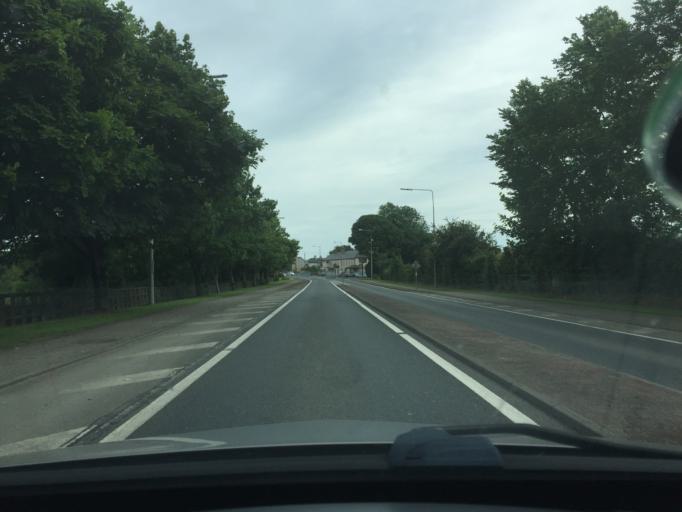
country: IE
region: Leinster
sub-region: Loch Garman
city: Enniscorthy
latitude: 52.4260
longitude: -6.5317
